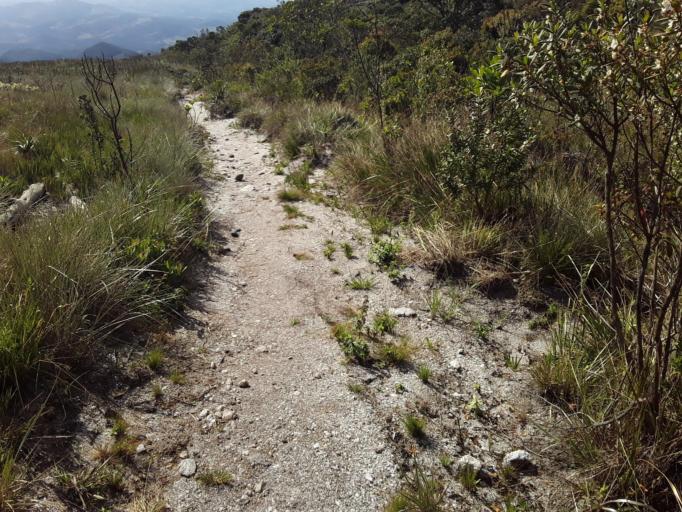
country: BR
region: Minas Gerais
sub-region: Lima Duarte
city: Lima Duarte
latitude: -21.6774
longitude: -43.8832
